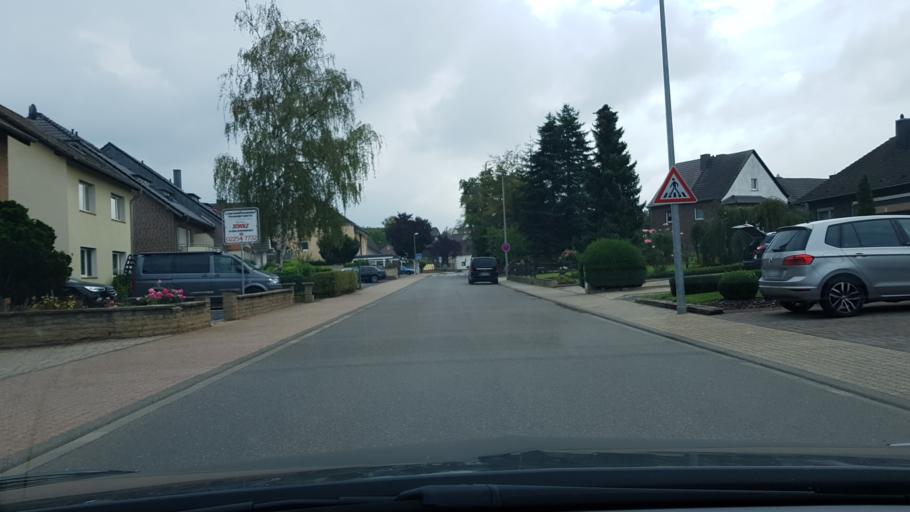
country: DE
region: North Rhine-Westphalia
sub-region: Regierungsbezirk Koln
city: Weilerswist
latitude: 50.7577
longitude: 6.8358
